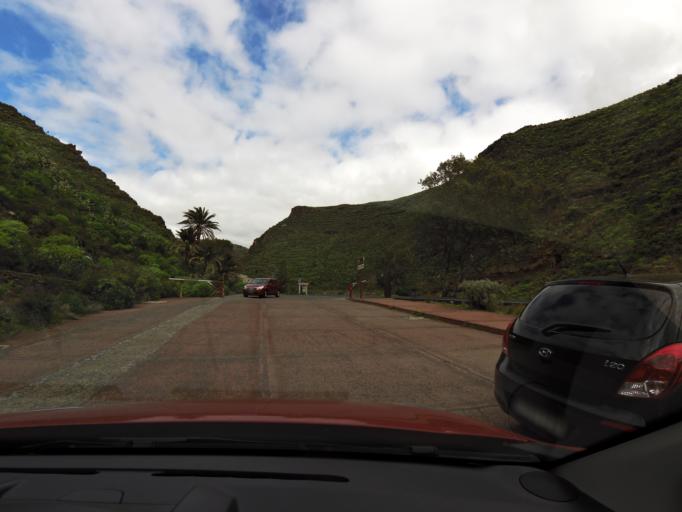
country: ES
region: Canary Islands
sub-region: Provincia de Las Palmas
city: Ingenio
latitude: 27.9241
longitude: -15.4611
